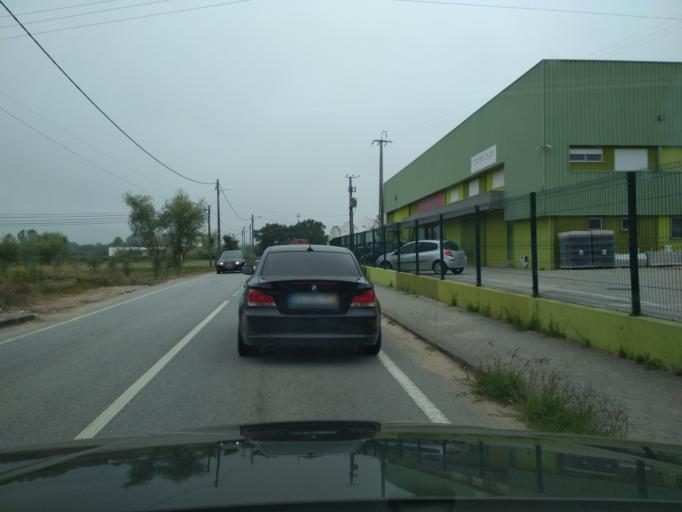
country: PT
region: Aveiro
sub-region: Mealhada
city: Mealhada
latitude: 40.3701
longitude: -8.4544
